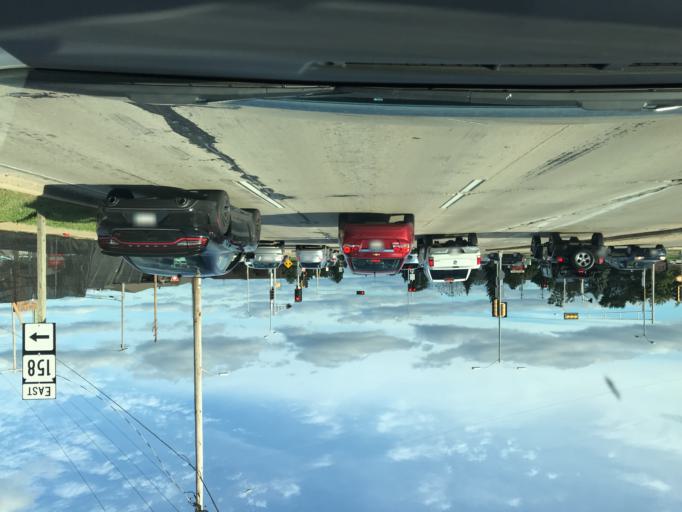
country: US
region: Wisconsin
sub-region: Kenosha County
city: Somers
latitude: 42.5881
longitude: -87.8824
